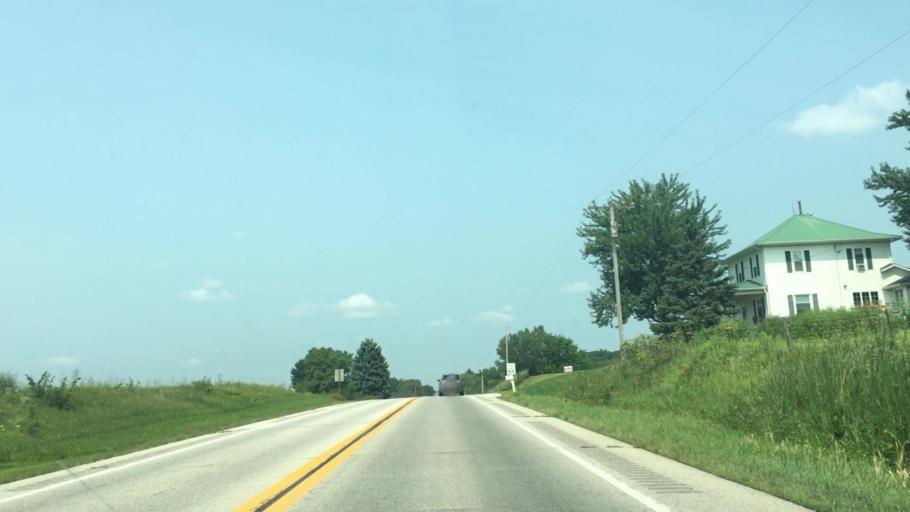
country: US
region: Iowa
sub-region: Buchanan County
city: Independence
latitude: 42.4889
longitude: -91.8895
